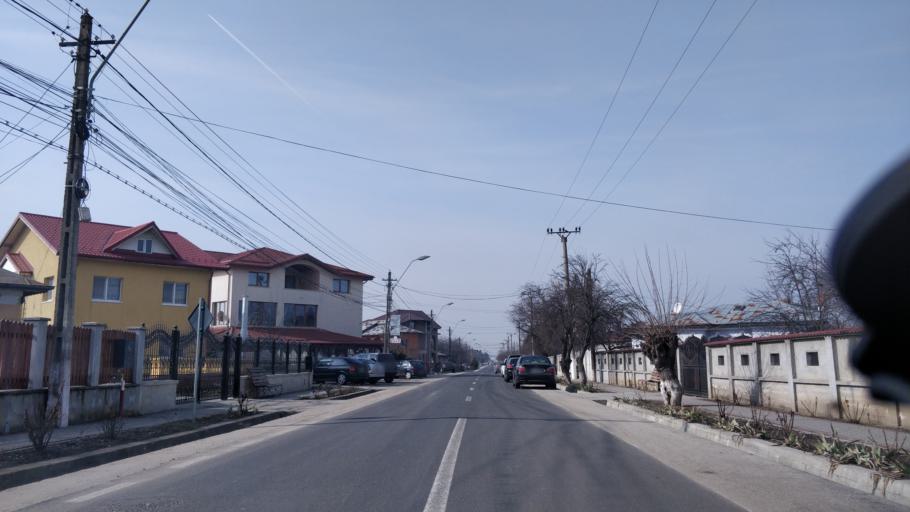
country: RO
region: Giurgiu
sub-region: Comuna Bolintin Deal
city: Bolintin Deal
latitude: 44.4598
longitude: 25.8144
